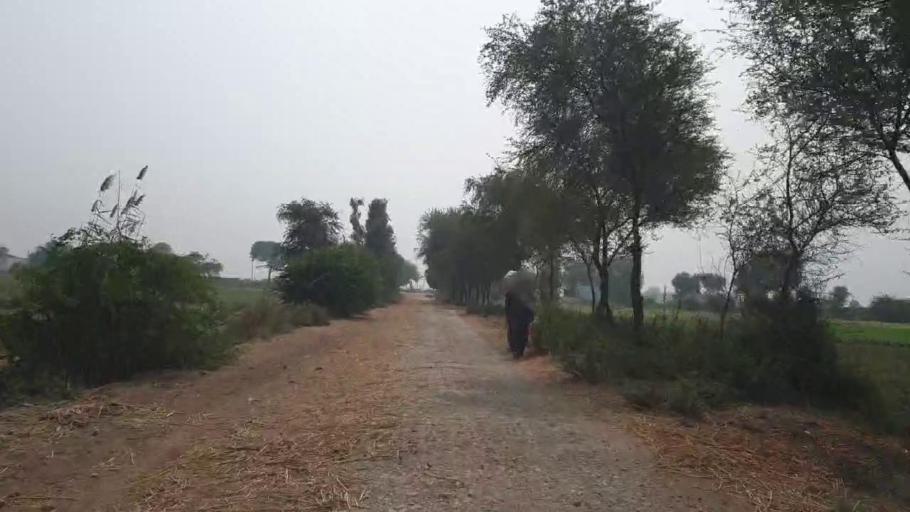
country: PK
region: Sindh
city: Kario
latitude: 24.6454
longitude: 68.6218
